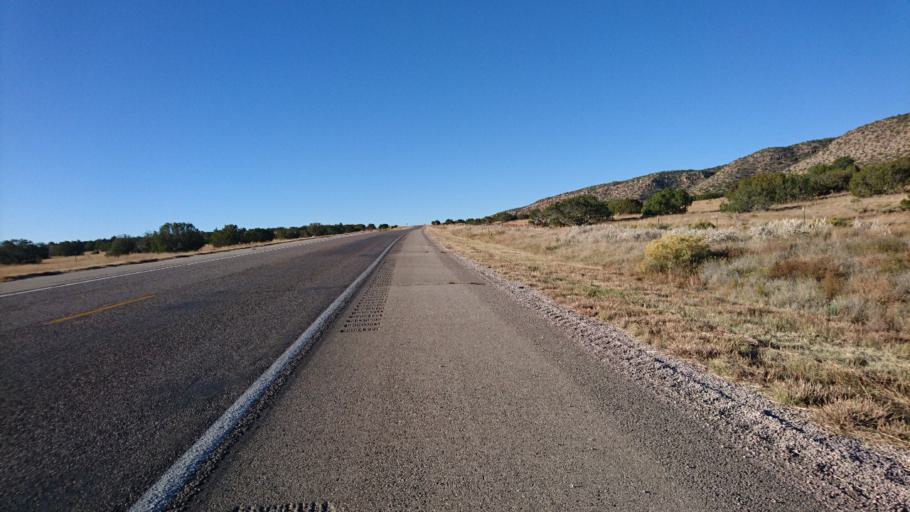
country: US
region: New Mexico
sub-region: Cibola County
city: Grants
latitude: 35.0055
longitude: -107.8924
